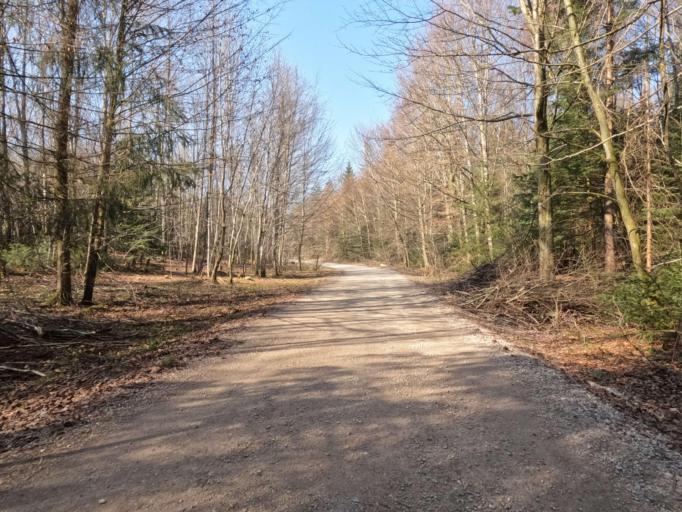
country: DE
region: Bavaria
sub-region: Upper Bavaria
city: Surberg
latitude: 47.8873
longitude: 12.6833
